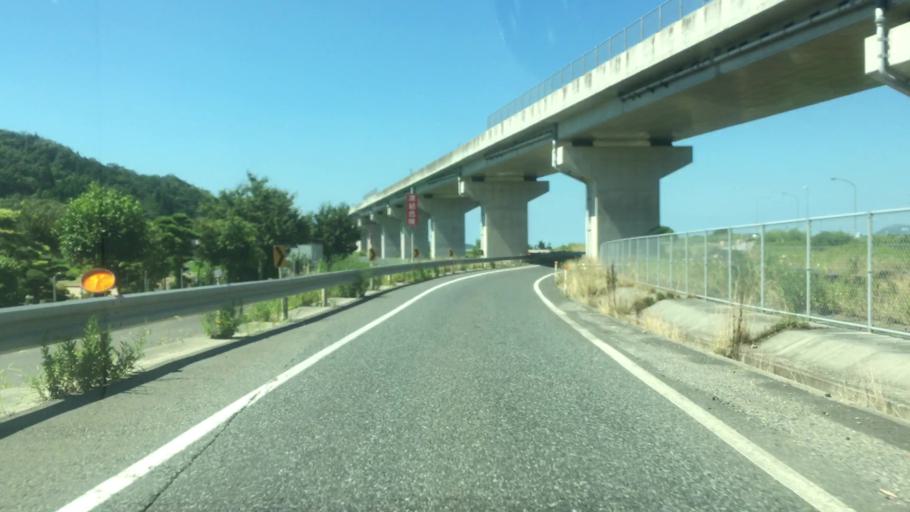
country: JP
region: Tottori
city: Tottori
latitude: 35.4343
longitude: 134.2045
